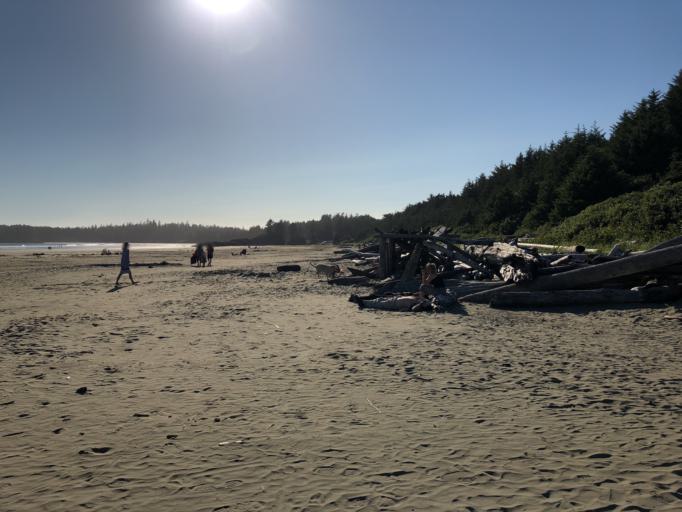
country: CA
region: British Columbia
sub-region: Regional District of Alberni-Clayoquot
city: Tofino
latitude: 49.0711
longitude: -125.7589
